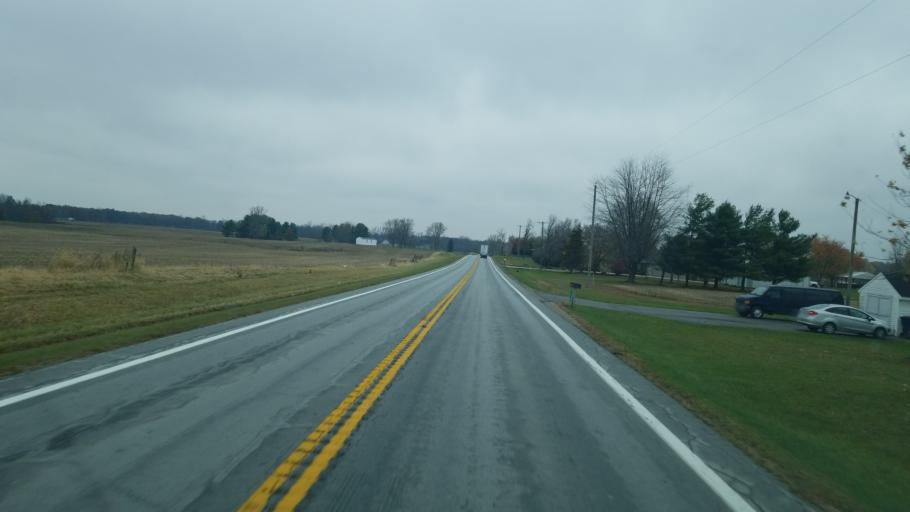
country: US
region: Ohio
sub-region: Union County
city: Marysville
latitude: 40.2974
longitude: -83.3398
